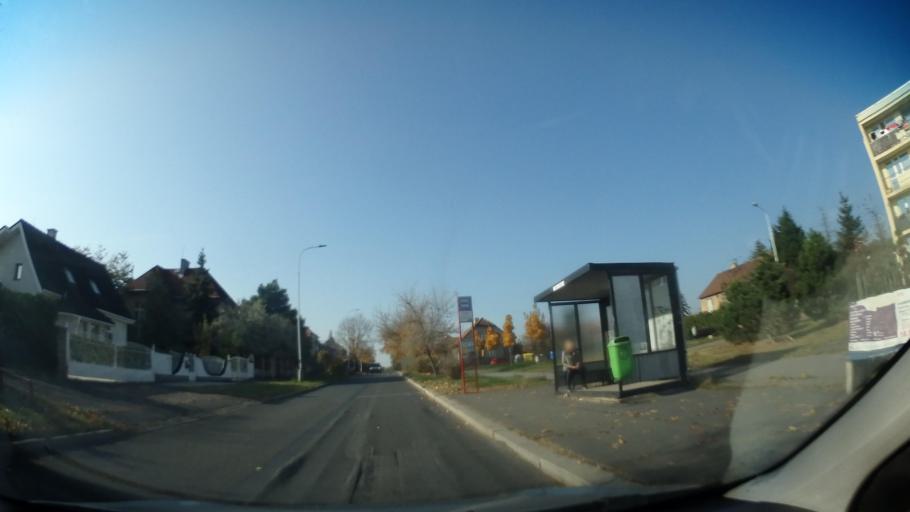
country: CZ
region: Praha
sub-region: Praha 14
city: Hostavice
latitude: 50.0933
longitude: 14.5408
